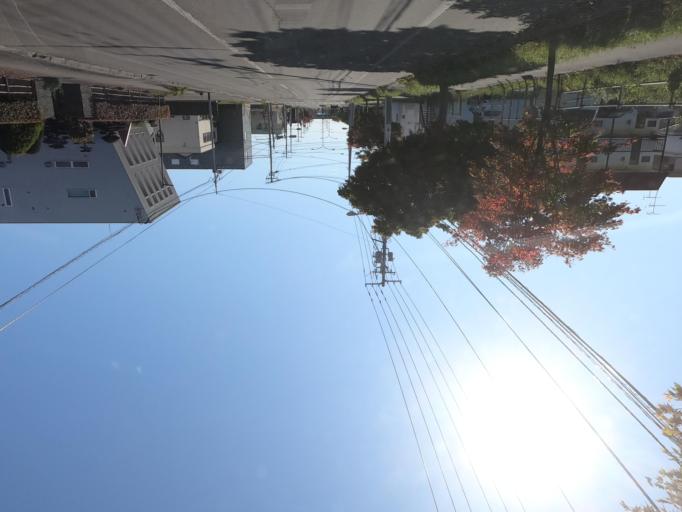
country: JP
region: Hokkaido
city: Obihiro
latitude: 42.9185
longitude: 143.2121
